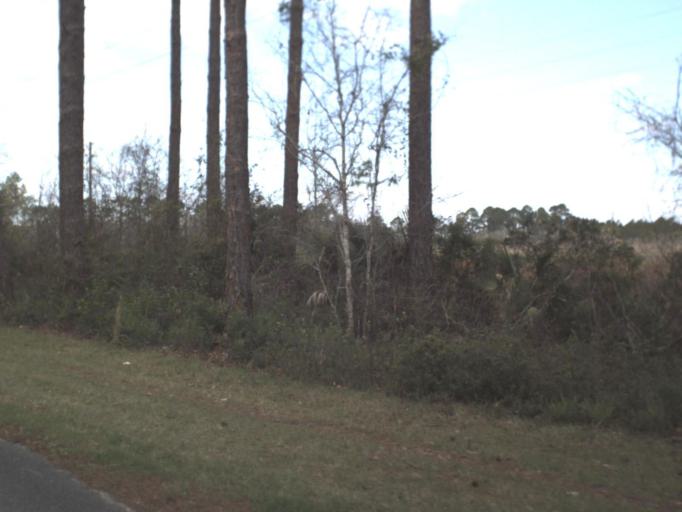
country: US
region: Florida
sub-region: Franklin County
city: Apalachicola
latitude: 29.7156
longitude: -85.0340
